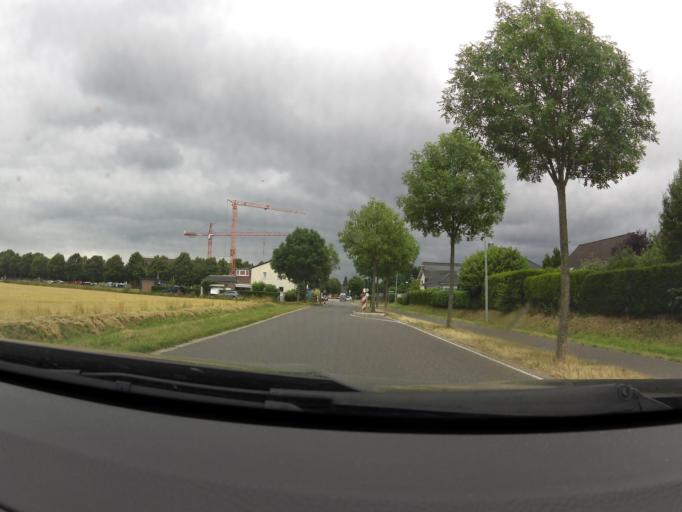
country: DE
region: North Rhine-Westphalia
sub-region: Regierungsbezirk Dusseldorf
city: Kevelaer
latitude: 51.5751
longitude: 6.2374
